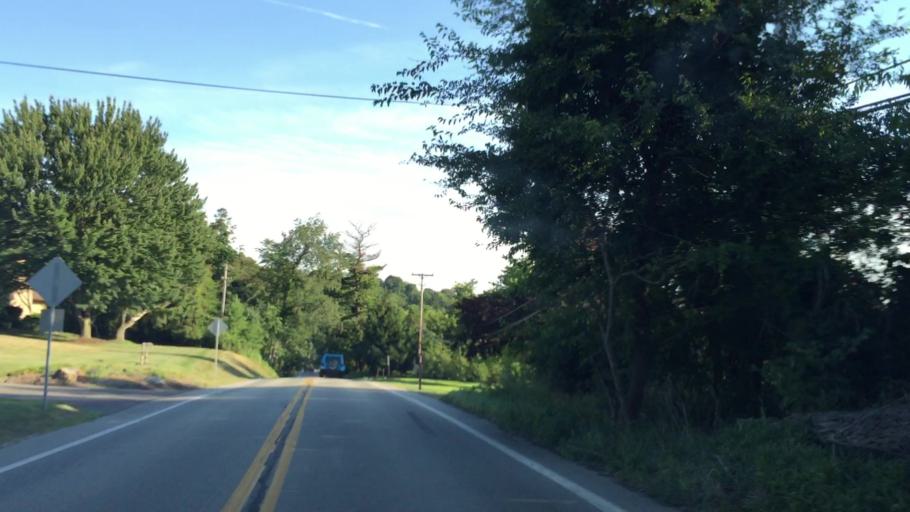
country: US
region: Pennsylvania
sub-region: Allegheny County
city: Franklin Park
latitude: 40.5663
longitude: -80.0785
